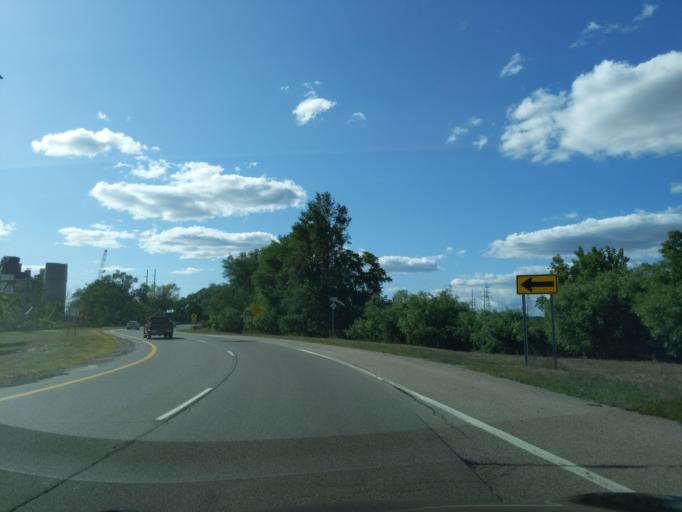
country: US
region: Michigan
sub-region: Muskegon County
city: Muskegon
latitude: 43.2534
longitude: -86.2334
